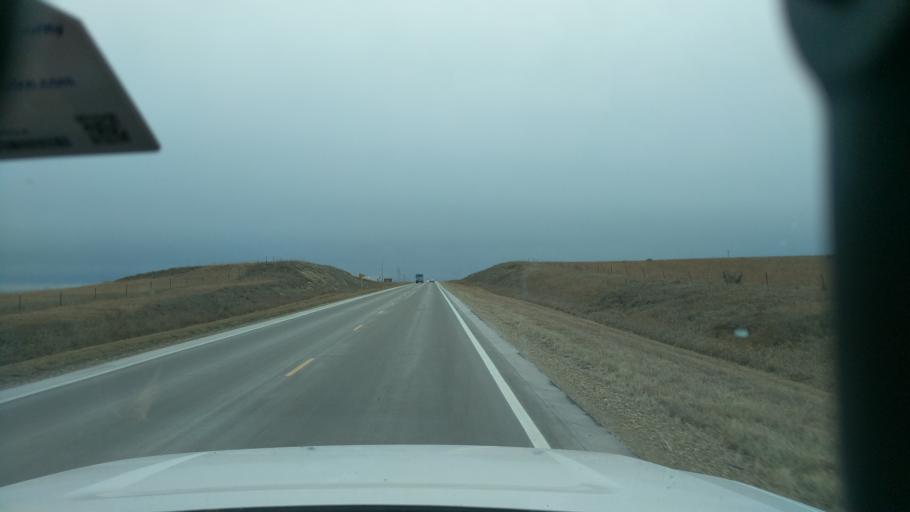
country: US
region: Kansas
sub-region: Dickinson County
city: Herington
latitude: 38.6887
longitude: -96.9305
